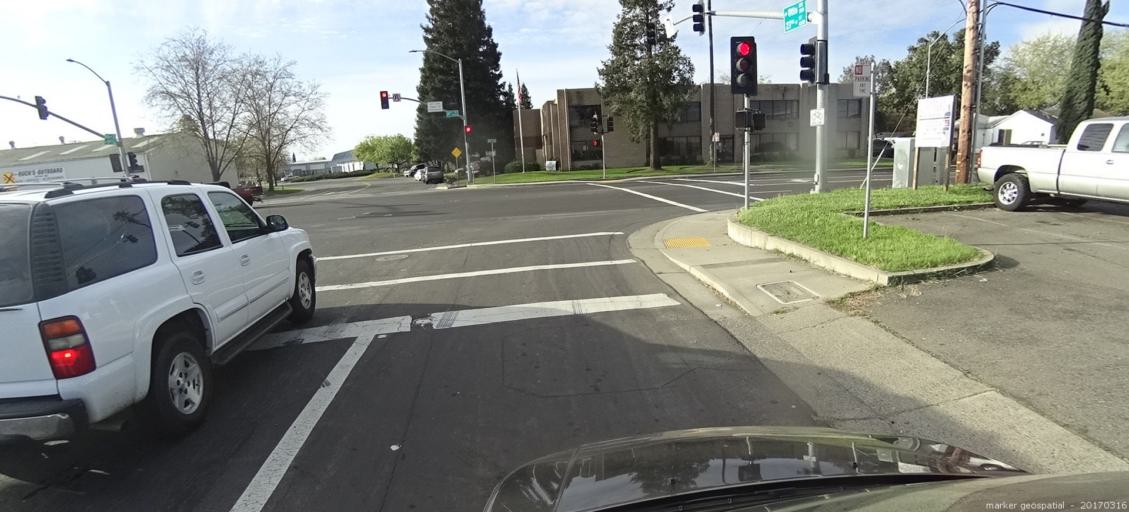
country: US
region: California
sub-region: Sacramento County
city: Parkway
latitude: 38.5105
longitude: -121.4773
